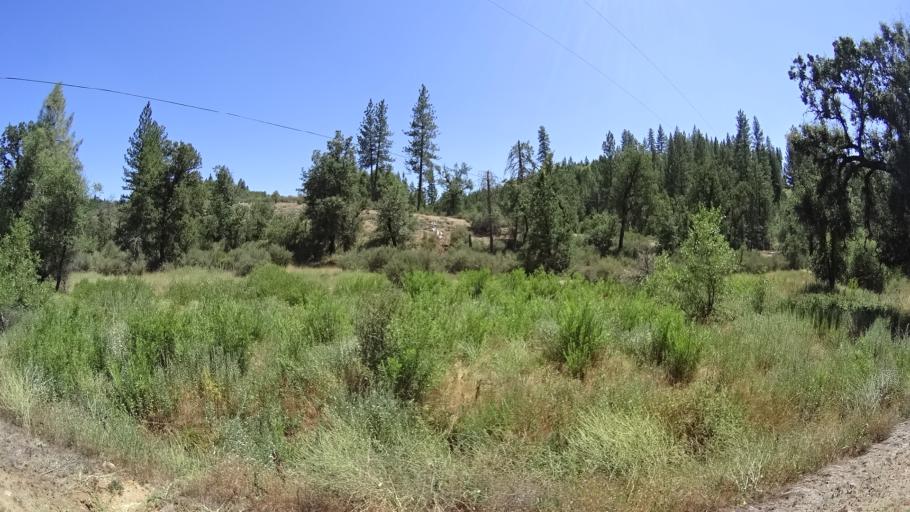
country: US
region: California
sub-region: Calaveras County
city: Mountain Ranch
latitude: 38.2962
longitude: -120.4940
